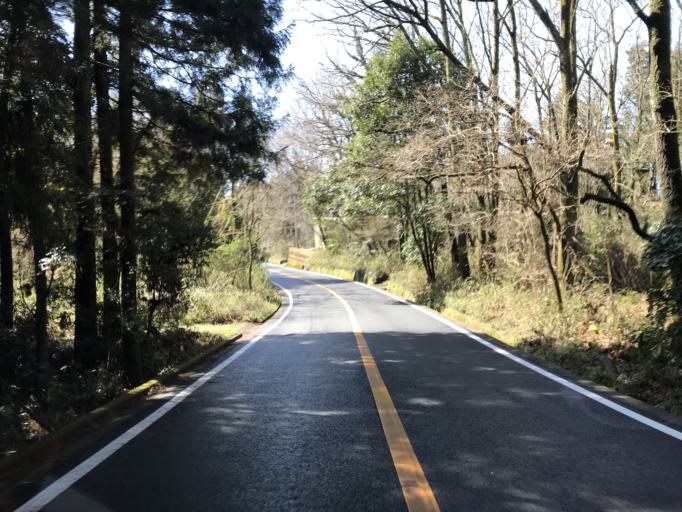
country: JP
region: Shizuoka
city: Fujinomiya
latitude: 35.2324
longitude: 138.6516
